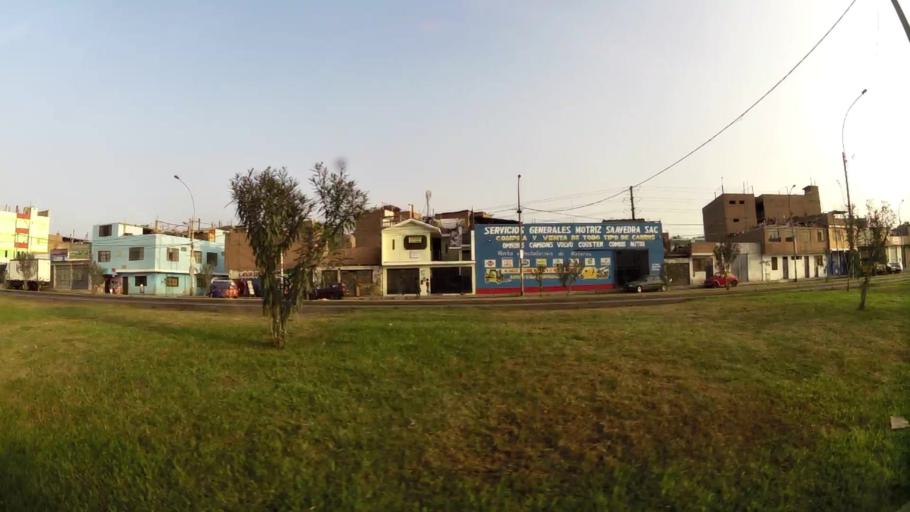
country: PE
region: Lima
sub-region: Lima
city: Independencia
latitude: -11.9903
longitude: -77.0953
